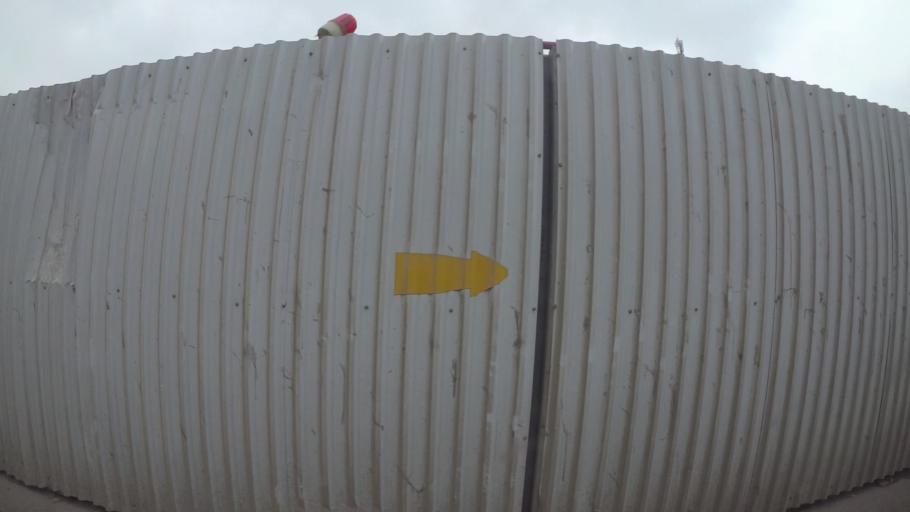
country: VN
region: Ha Noi
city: Tay Ho
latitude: 21.0786
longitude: 105.7875
